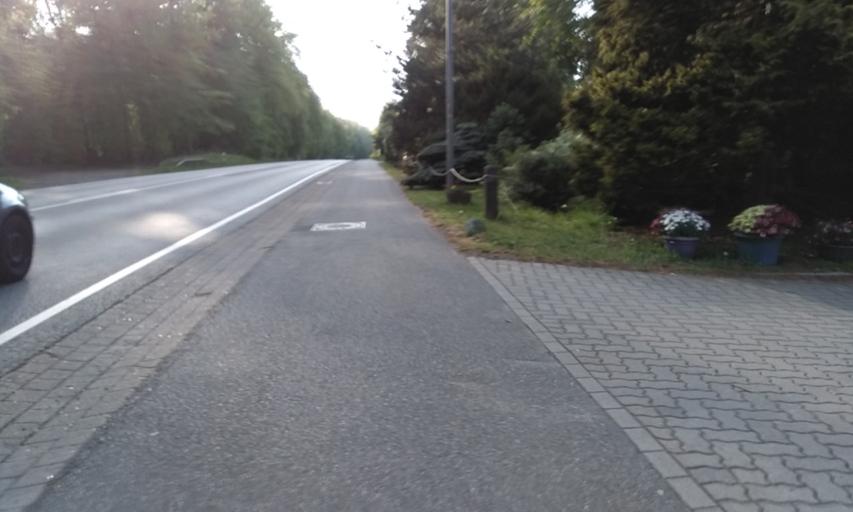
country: DE
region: Lower Saxony
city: Buxtehude
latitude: 53.4726
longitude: 9.6582
